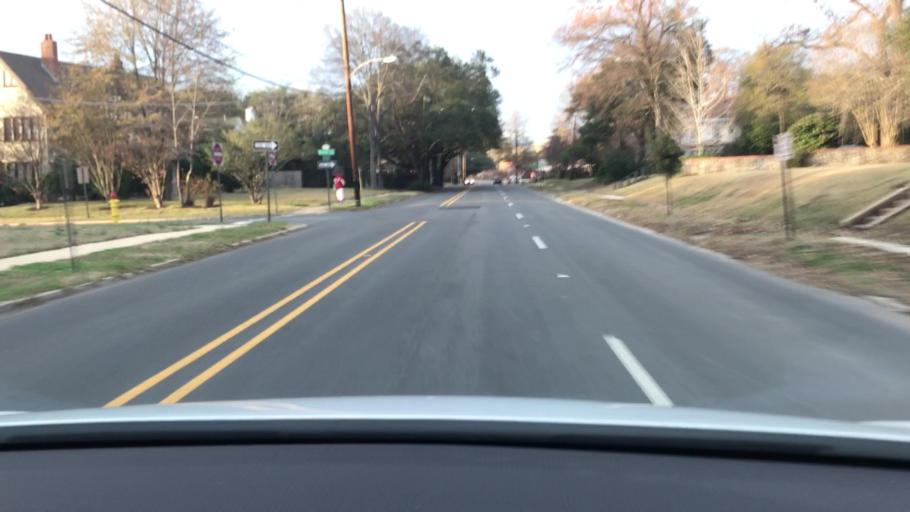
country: US
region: Louisiana
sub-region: Bossier Parish
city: Bossier City
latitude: 32.4889
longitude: -93.7502
